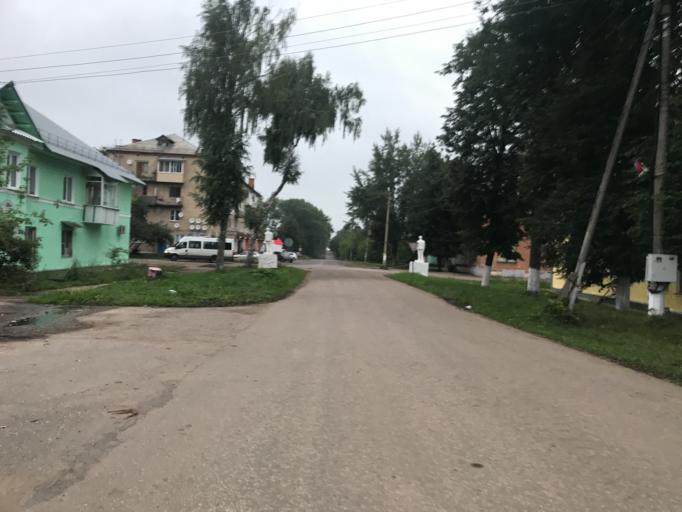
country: RU
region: Tula
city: Priupskiy
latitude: 53.9459
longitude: 37.7013
